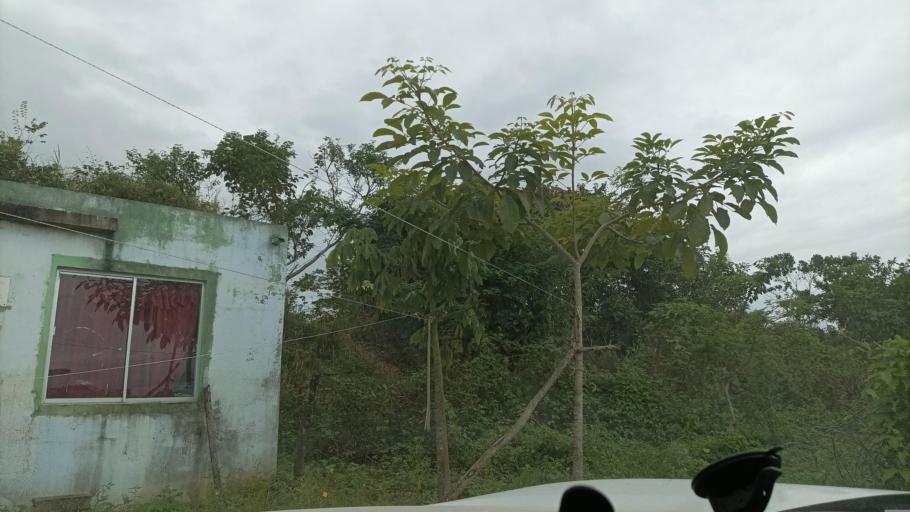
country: MX
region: Veracruz
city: Hidalgotitlan
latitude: 17.7703
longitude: -94.6535
